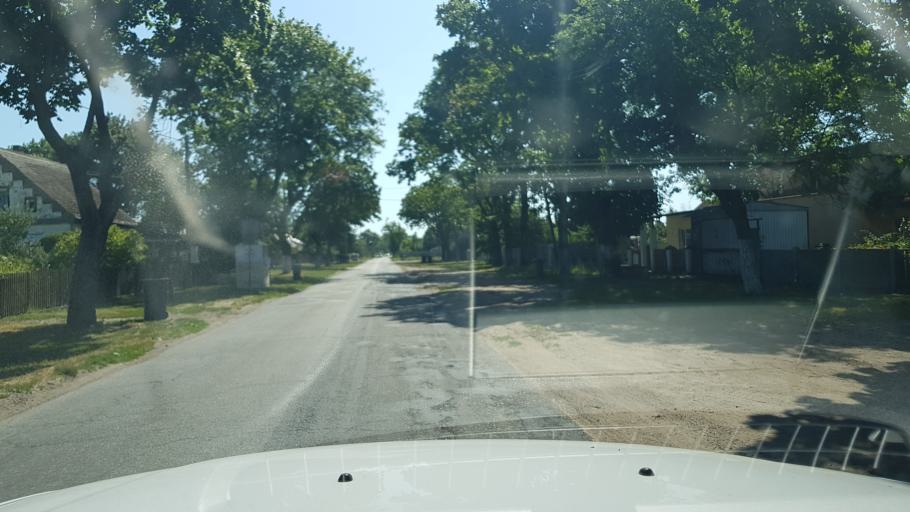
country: PL
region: West Pomeranian Voivodeship
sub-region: Powiat goleniowski
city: Goleniow
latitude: 53.4584
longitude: 14.7215
